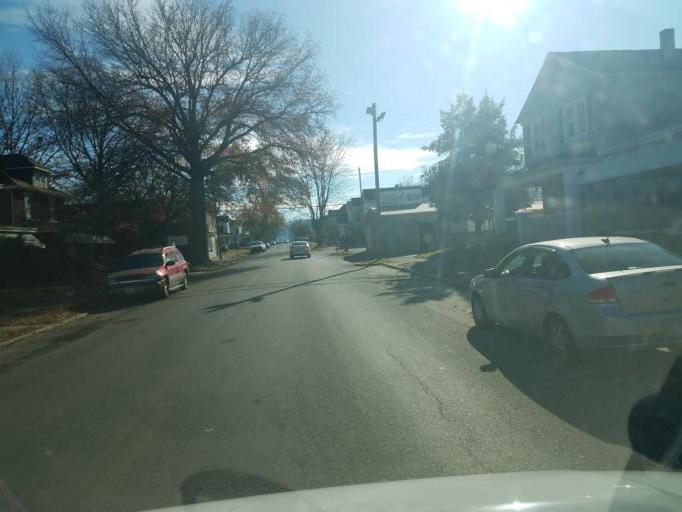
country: US
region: Ohio
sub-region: Scioto County
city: Portsmouth
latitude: 38.7448
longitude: -82.9751
